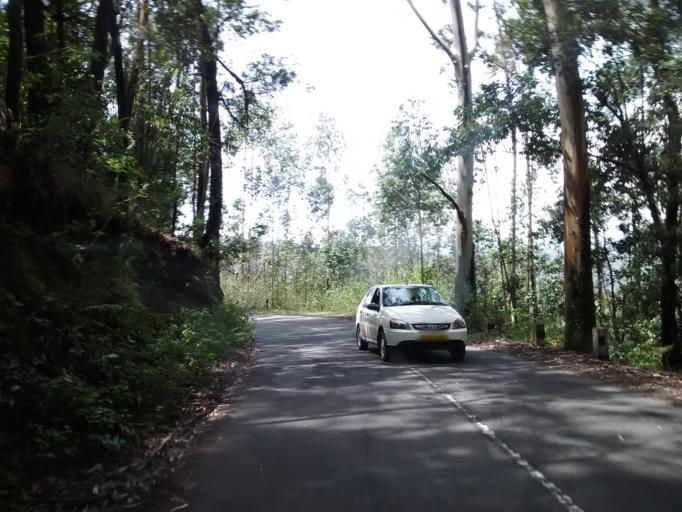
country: IN
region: Kerala
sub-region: Idukki
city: Munnar
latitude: 10.0997
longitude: 77.1121
